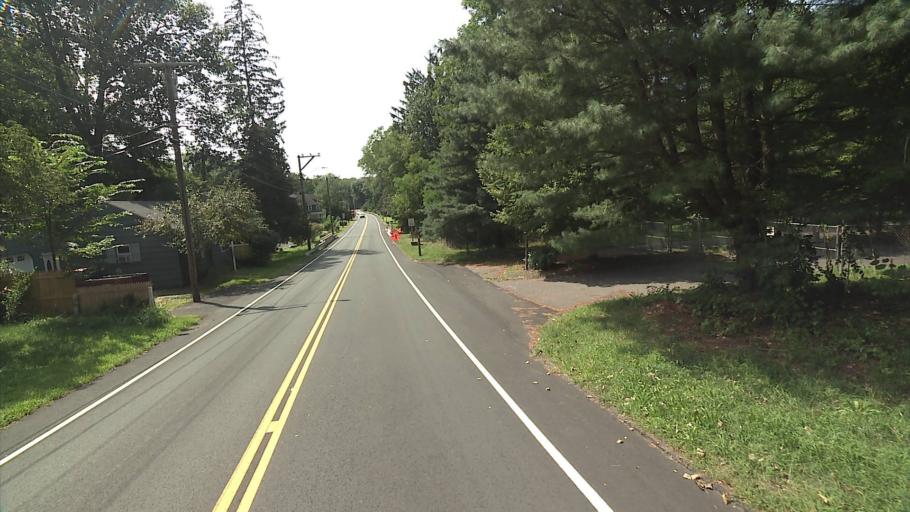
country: US
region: Connecticut
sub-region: Hartford County
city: Broad Brook
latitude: 41.9148
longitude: -72.5466
